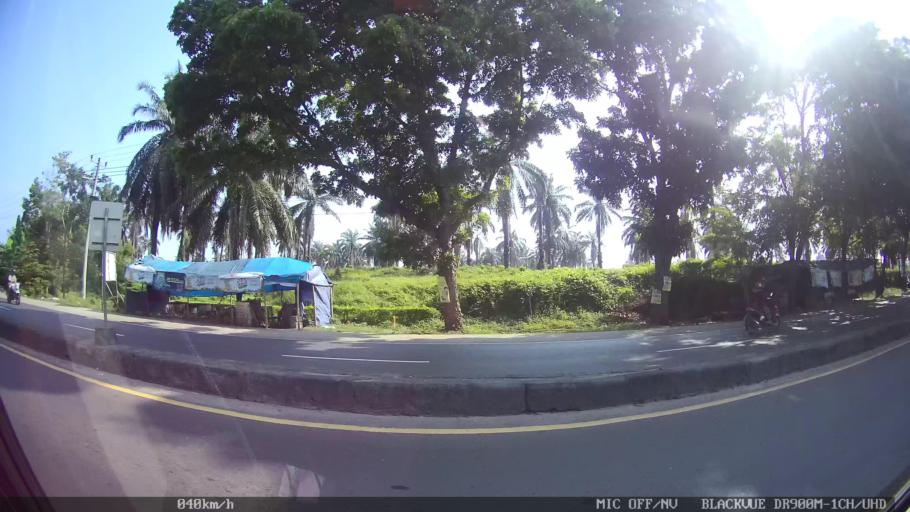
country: ID
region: Lampung
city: Natar
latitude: -5.3271
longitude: 105.2034
